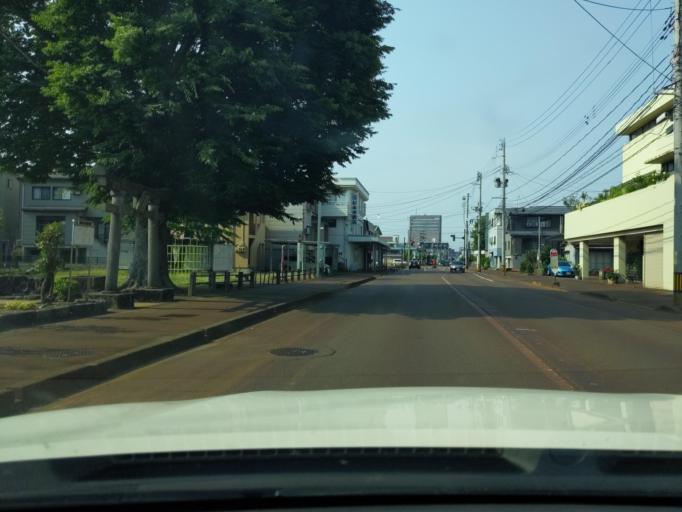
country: JP
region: Niigata
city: Nagaoka
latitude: 37.4404
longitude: 138.8556
